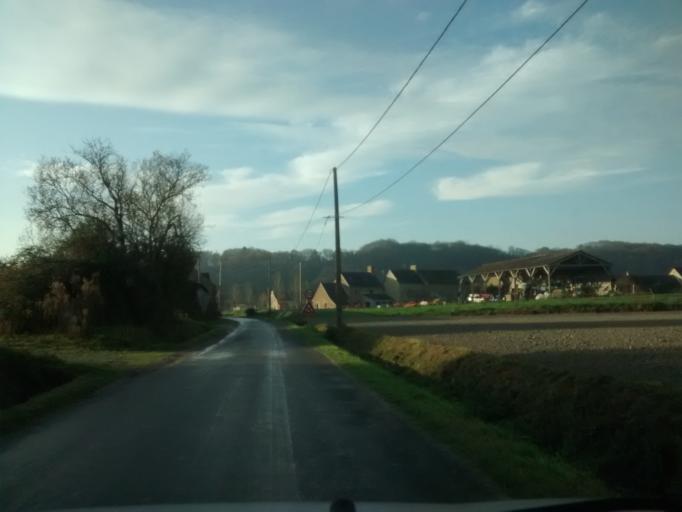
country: FR
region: Brittany
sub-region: Departement d'Ille-et-Vilaine
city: Roz-sur-Couesnon
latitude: 48.5972
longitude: -1.5885
